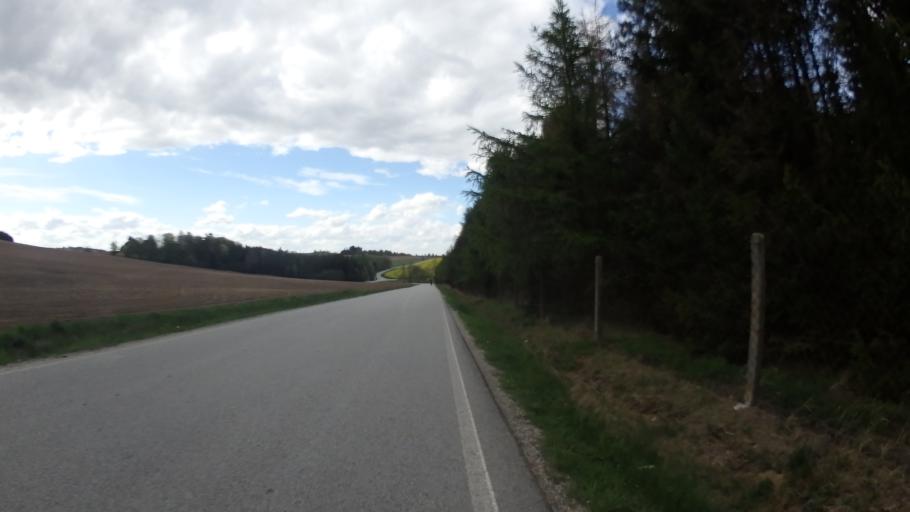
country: CZ
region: Vysocina
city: Merin
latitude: 49.3707
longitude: 15.8960
